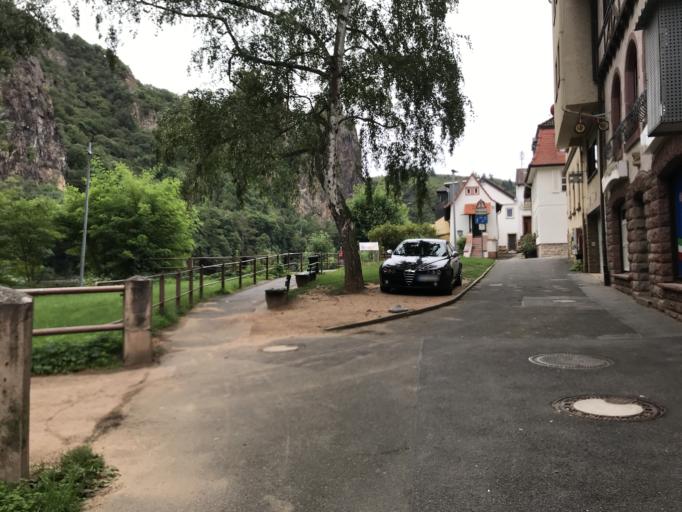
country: DE
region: Rheinland-Pfalz
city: Bad Munster am Stein-Ebernburg
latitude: 49.8116
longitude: 7.8493
